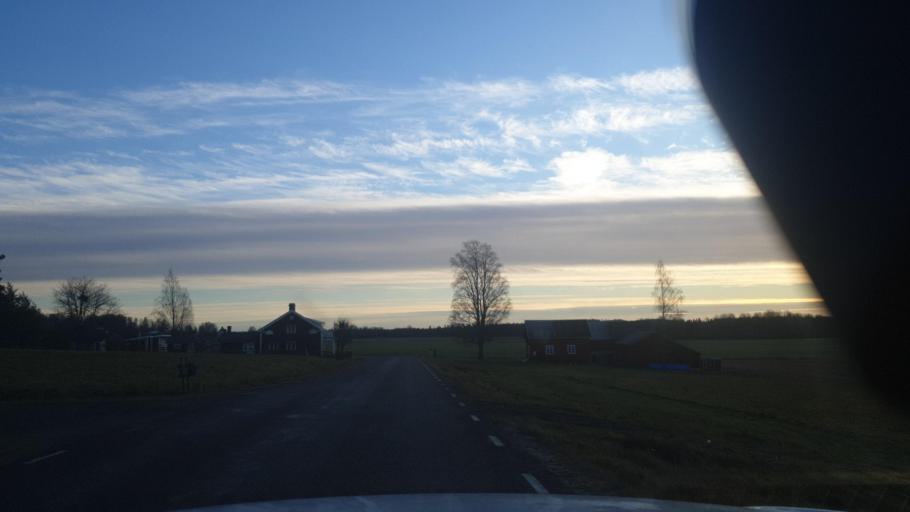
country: SE
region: Vaermland
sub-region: Sunne Kommun
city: Sunne
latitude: 59.7427
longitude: 13.0910
